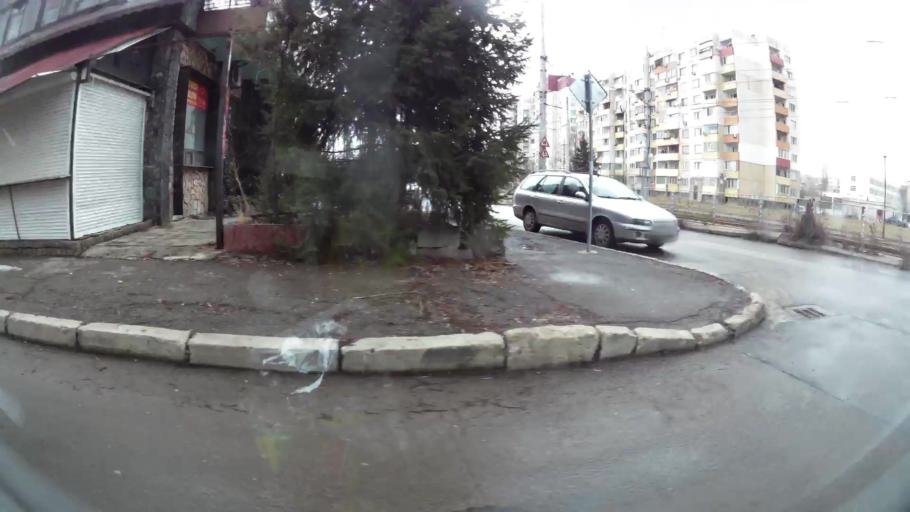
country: BG
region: Sofia-Capital
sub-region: Stolichna Obshtina
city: Sofia
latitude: 42.7344
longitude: 23.2865
